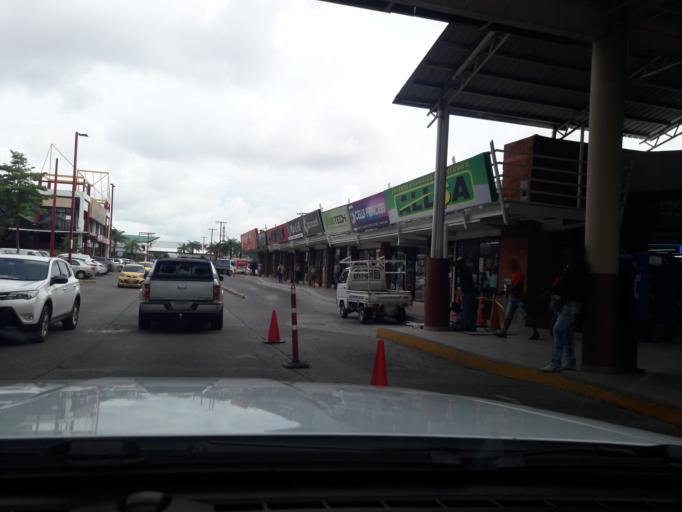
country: PA
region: Panama
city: San Miguelito
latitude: 9.0495
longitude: -79.5079
